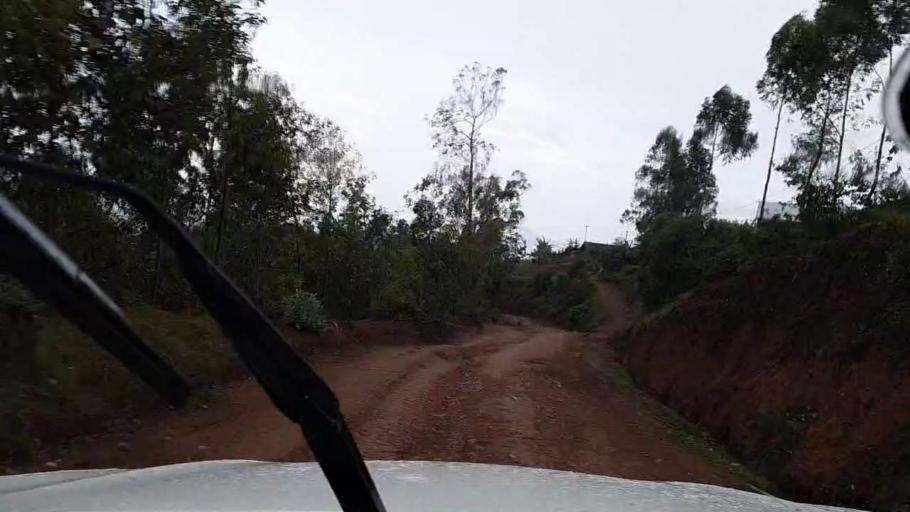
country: BI
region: Kayanza
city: Kayanza
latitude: -2.7825
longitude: 29.5334
